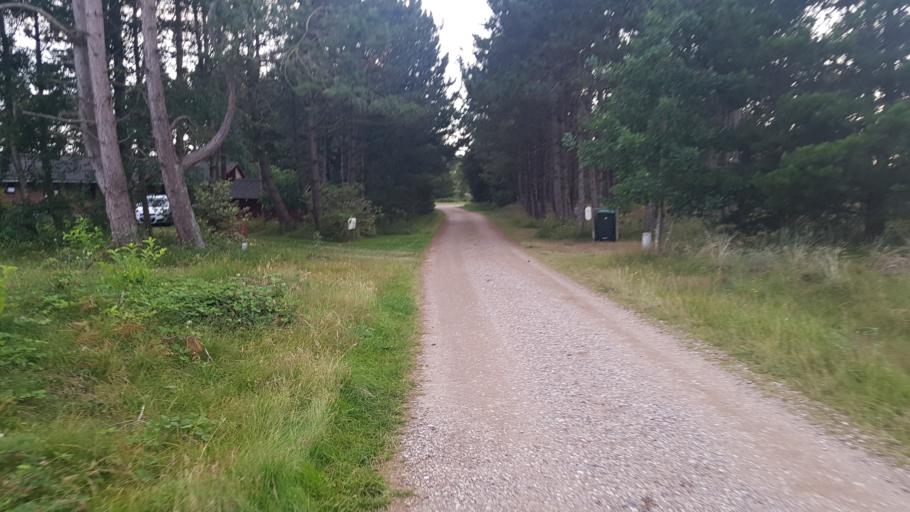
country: DE
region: Schleswig-Holstein
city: List
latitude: 55.0927
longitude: 8.5316
